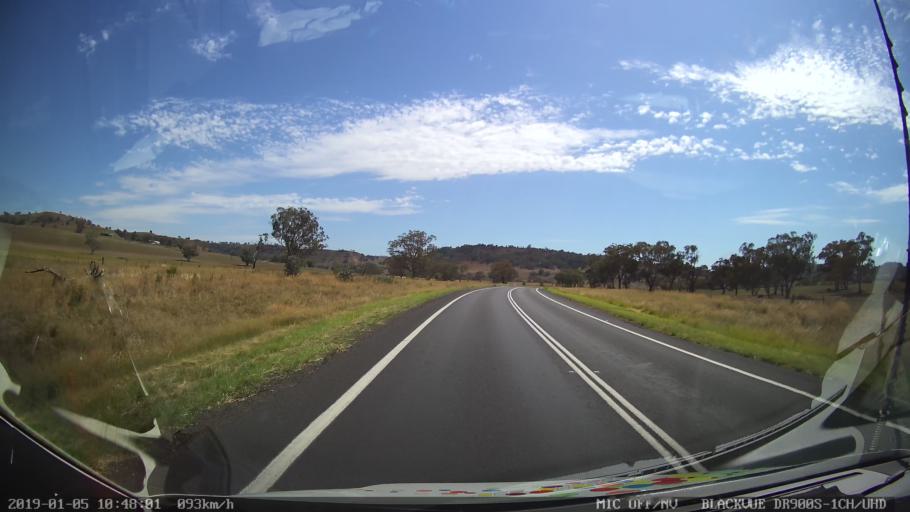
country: AU
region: New South Wales
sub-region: Warrumbungle Shire
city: Coonabarabran
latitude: -31.4399
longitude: 149.0404
